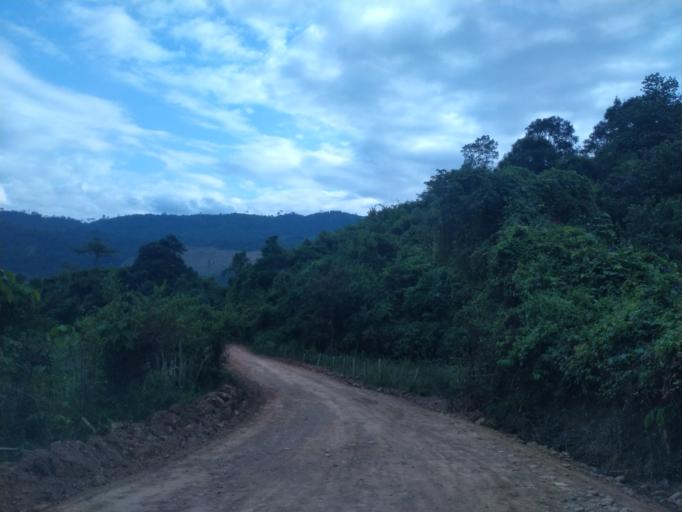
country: TH
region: Nong Khai
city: Rattanawapi
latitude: 18.5433
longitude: 102.8968
